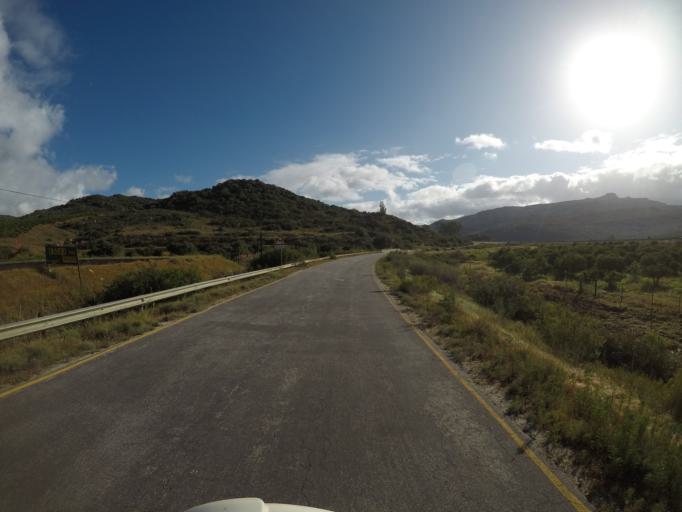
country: ZA
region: Western Cape
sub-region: West Coast District Municipality
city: Clanwilliam
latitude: -32.4314
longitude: 18.9538
